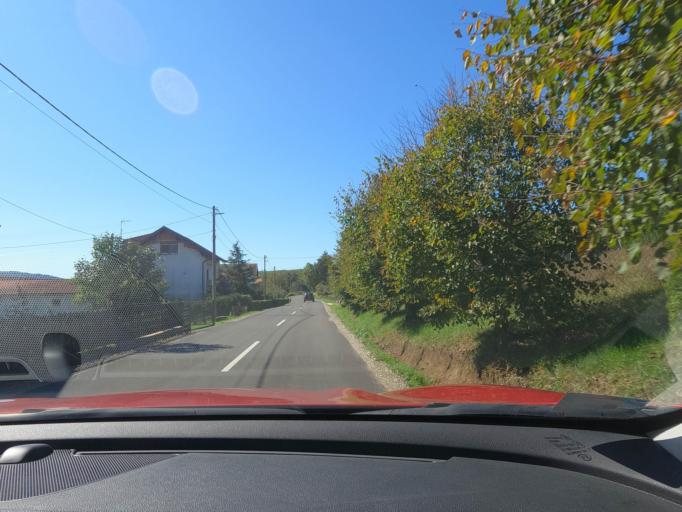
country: HR
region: Sisacko-Moslavacka
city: Petrinja
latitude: 45.4548
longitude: 16.2613
